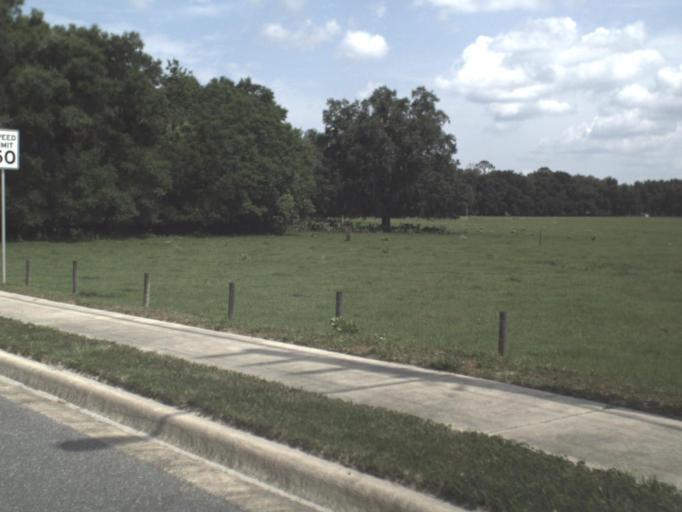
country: US
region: Florida
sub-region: Putnam County
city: Palatka
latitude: 29.6297
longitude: -81.7244
